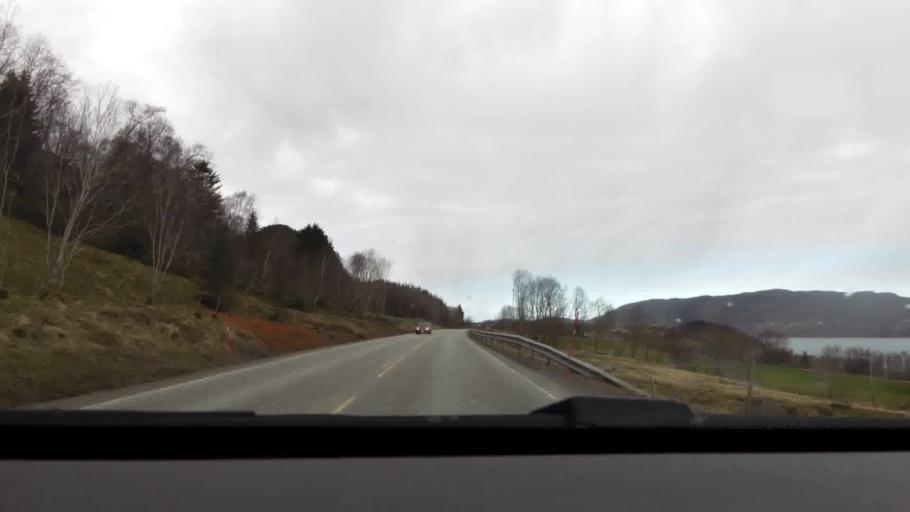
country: NO
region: More og Romsdal
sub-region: Kristiansund
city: Rensvik
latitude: 63.1089
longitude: 7.7847
